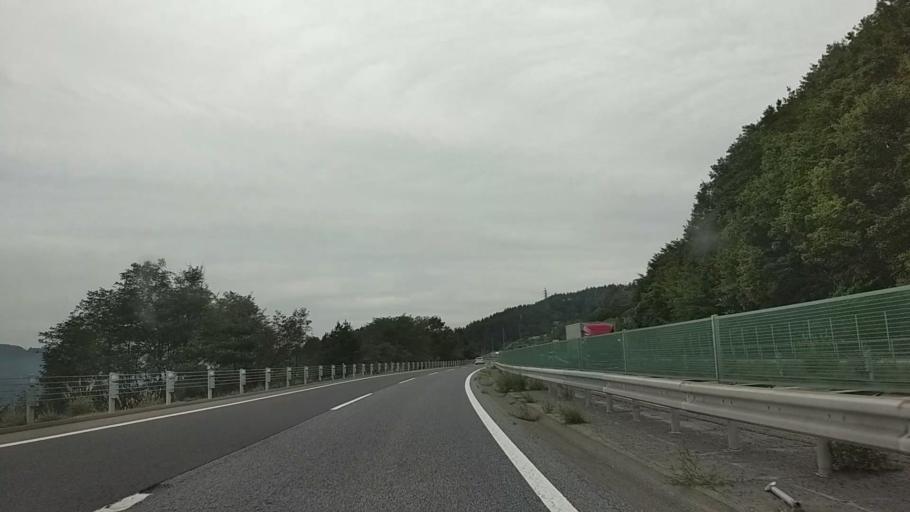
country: JP
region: Nagano
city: Hotaka
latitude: 36.4279
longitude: 138.0101
